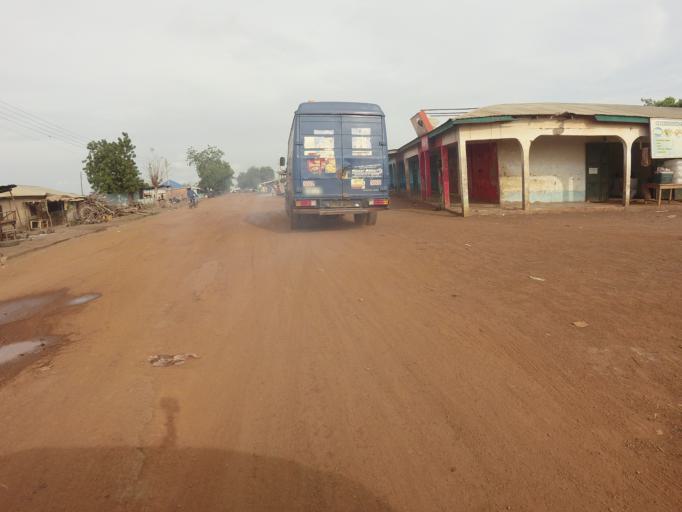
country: GH
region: Northern
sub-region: Yendi
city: Yendi
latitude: 9.9234
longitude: -0.2149
